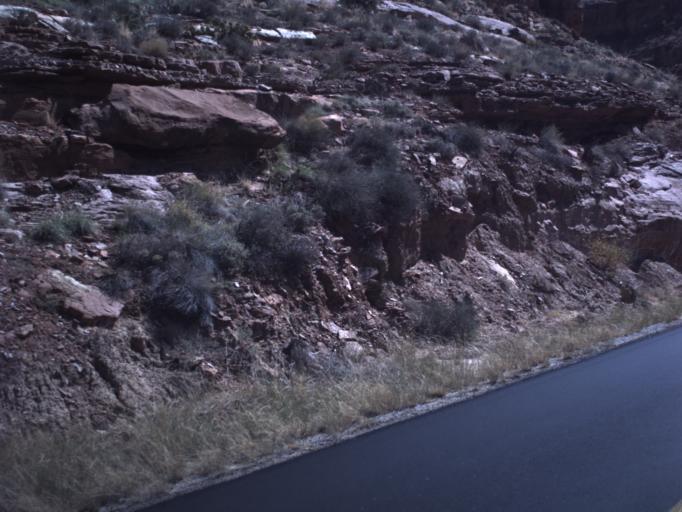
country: US
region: Utah
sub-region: Grand County
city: Moab
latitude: 38.6061
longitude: -109.5575
